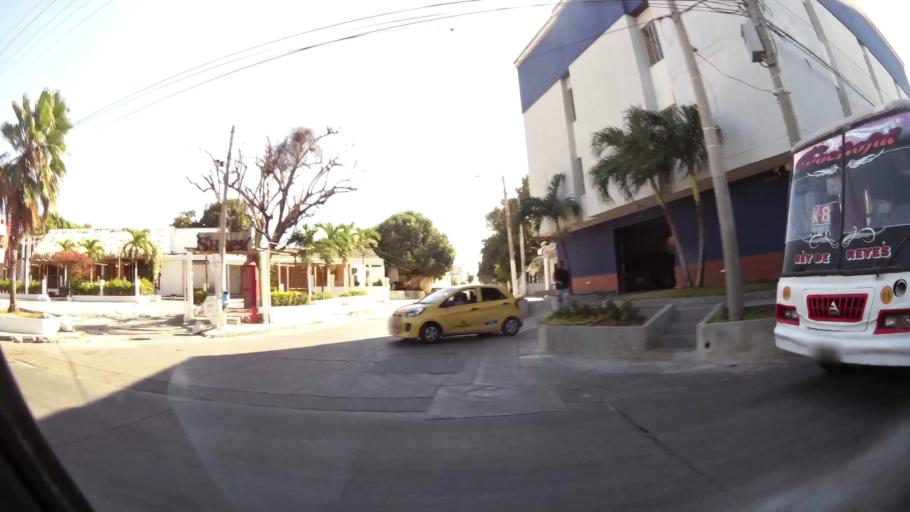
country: CO
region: Atlantico
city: Barranquilla
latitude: 10.9461
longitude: -74.7954
